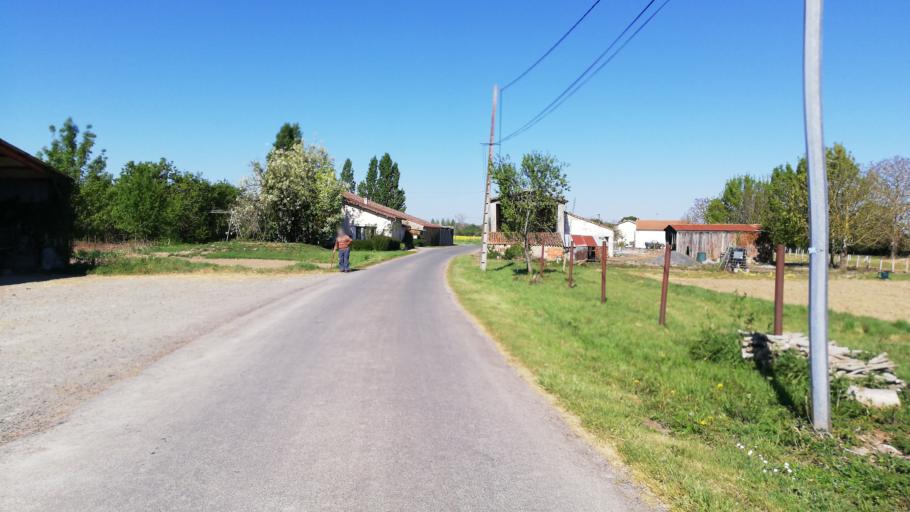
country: FR
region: Pays de la Loire
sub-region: Departement de la Vendee
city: Maillezais
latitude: 46.3261
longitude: -0.7445
